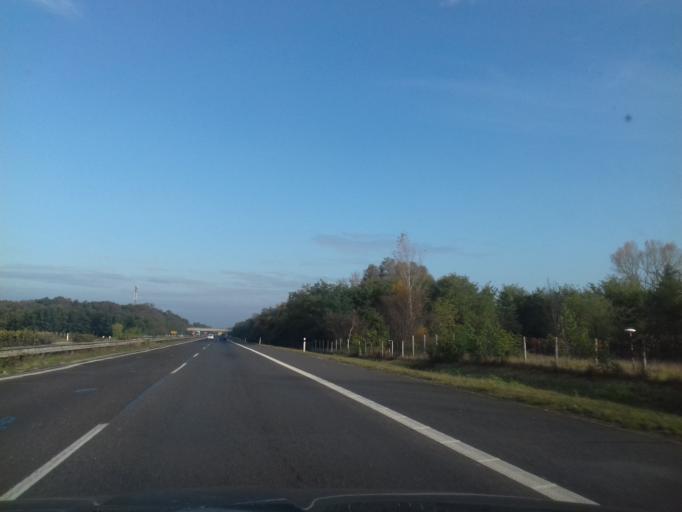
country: SK
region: Bratislavsky
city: Stupava
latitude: 48.3425
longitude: 17.0231
